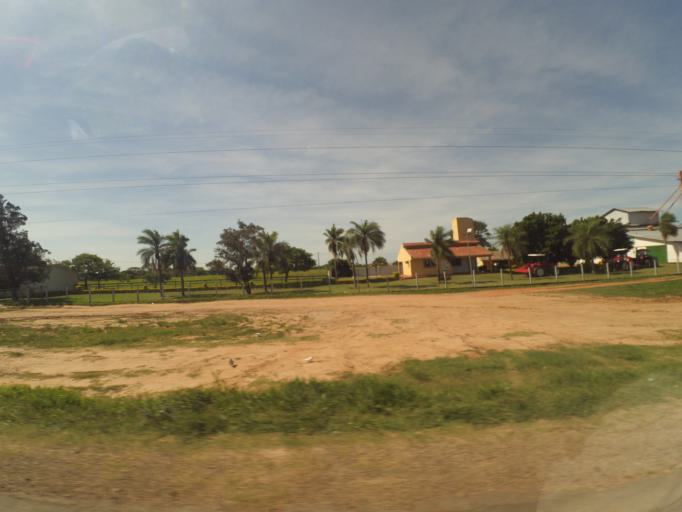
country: BO
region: Santa Cruz
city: Cotoca
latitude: -17.7514
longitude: -62.9793
